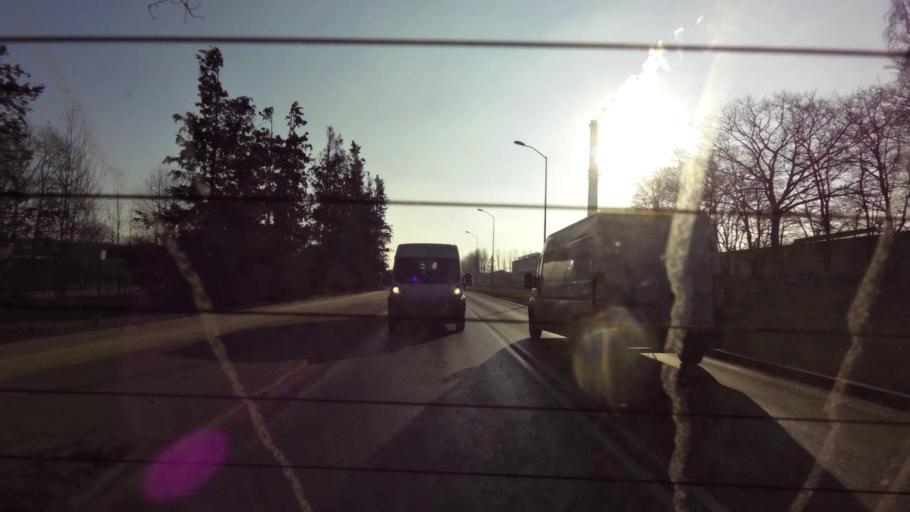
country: PL
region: West Pomeranian Voivodeship
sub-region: Koszalin
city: Koszalin
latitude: 54.1786
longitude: 16.1718
